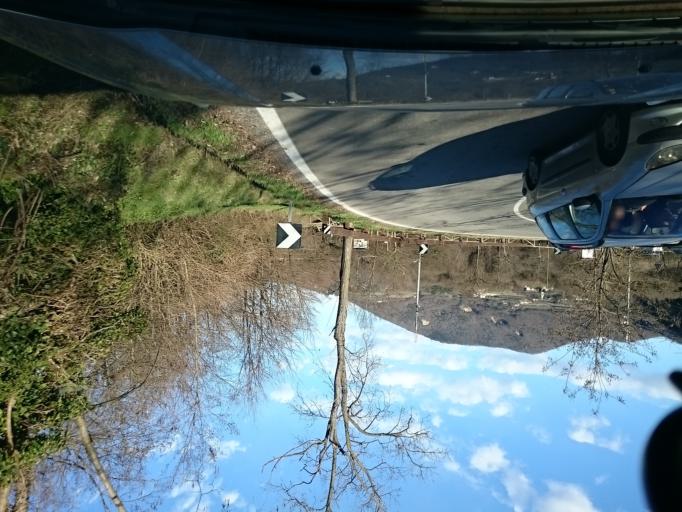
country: IT
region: Veneto
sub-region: Provincia di Padova
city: Vo
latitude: 45.3399
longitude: 11.6789
